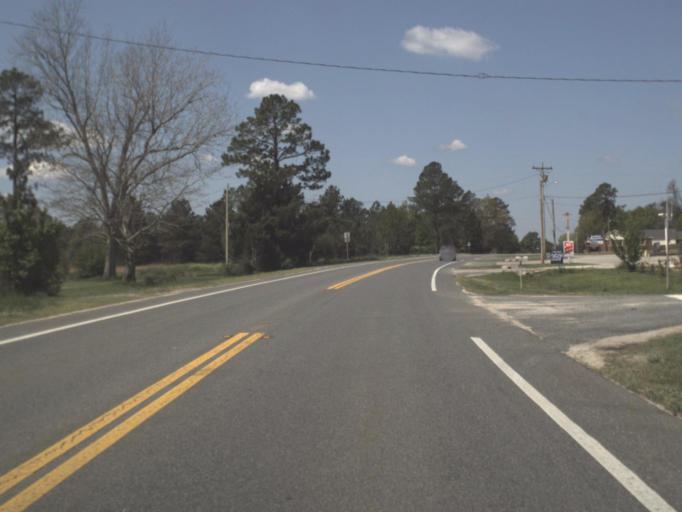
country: US
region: Florida
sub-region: Escambia County
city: Century
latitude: 30.9486
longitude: -87.1767
